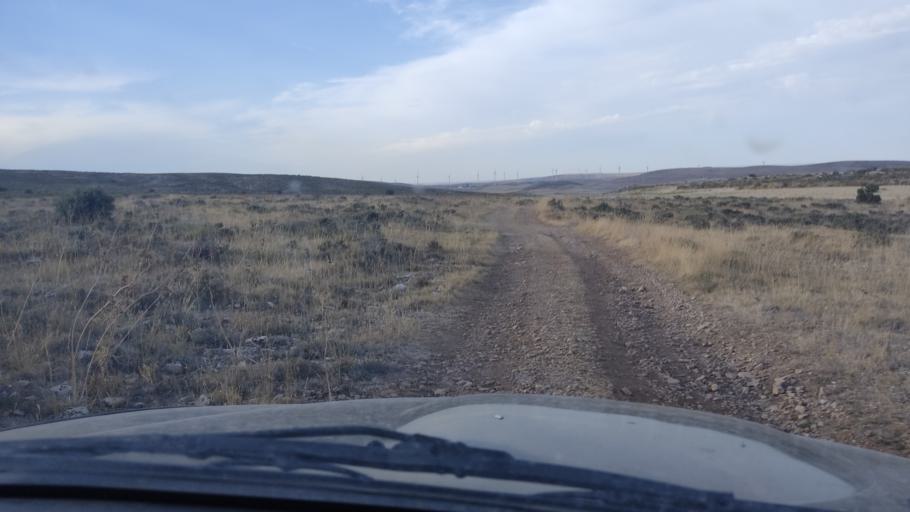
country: ES
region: Aragon
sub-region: Provincia de Teruel
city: Monforte de Moyuela
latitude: 41.0295
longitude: -0.9995
